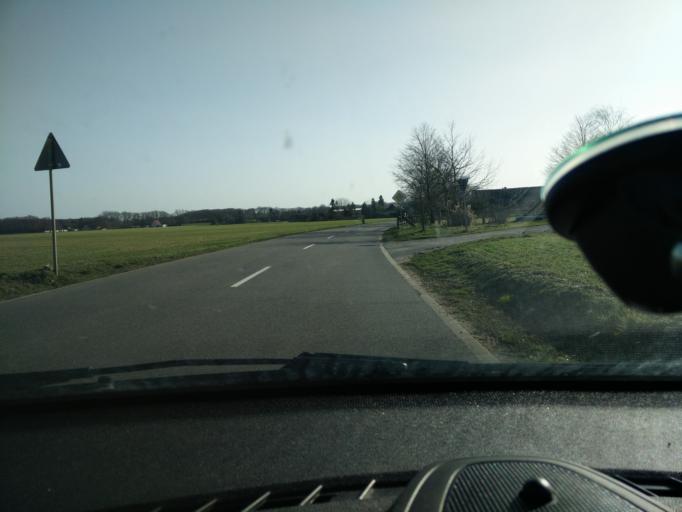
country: DE
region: North Rhine-Westphalia
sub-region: Regierungsbezirk Dusseldorf
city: Alpen
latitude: 51.5953
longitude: 6.4785
